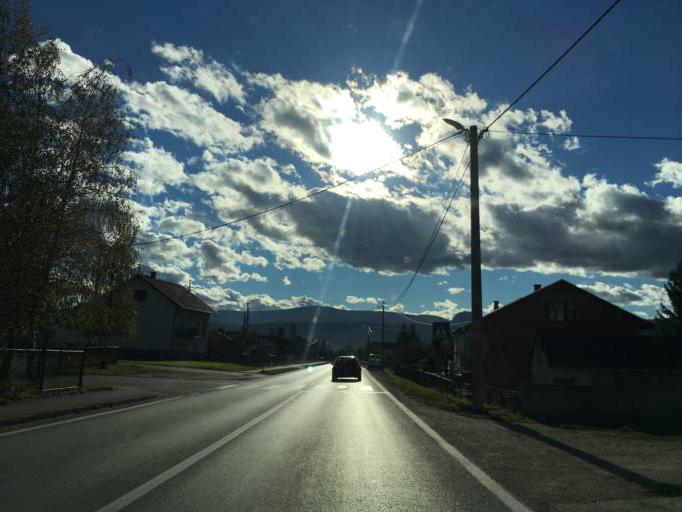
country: BA
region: Federation of Bosnia and Herzegovina
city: Bugojno
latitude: 44.0657
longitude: 17.4757
